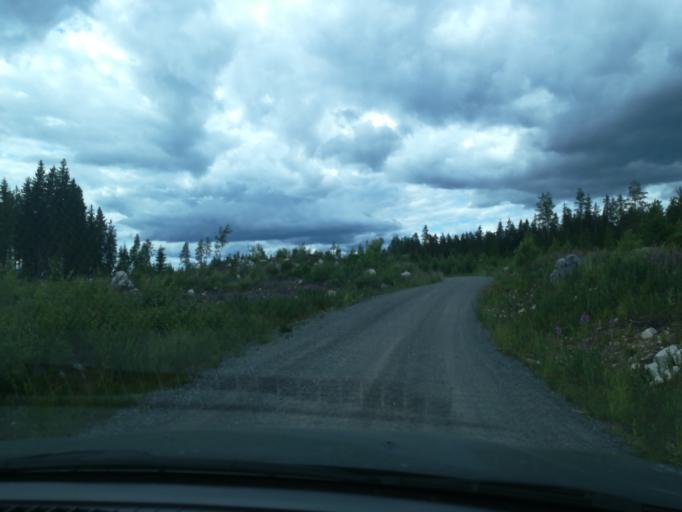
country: FI
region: Southern Savonia
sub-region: Mikkeli
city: Mikkeli
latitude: 61.6682
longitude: 27.1203
